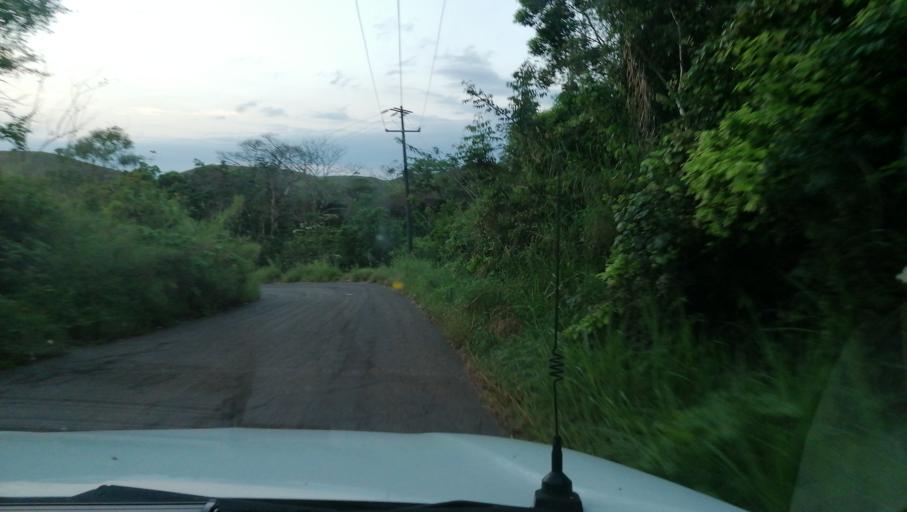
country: MX
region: Chiapas
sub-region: Ostuacan
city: Nuevo Juan del Grijalva
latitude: 17.4430
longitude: -93.3531
